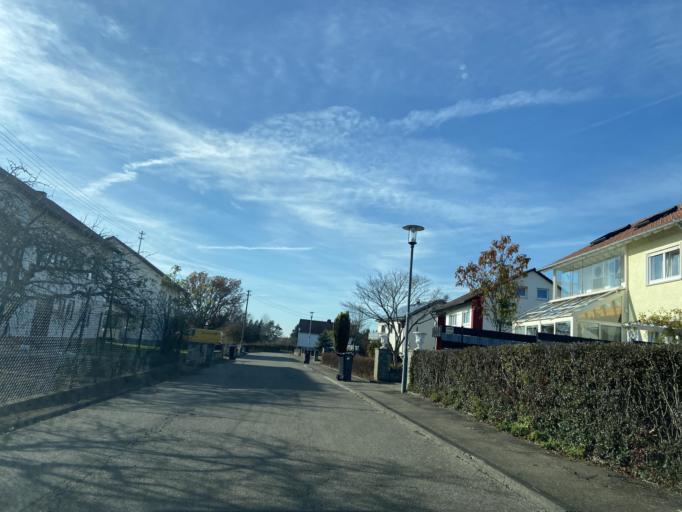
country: DE
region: Baden-Wuerttemberg
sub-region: Tuebingen Region
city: Schwenningen
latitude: 48.1158
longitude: 9.0292
